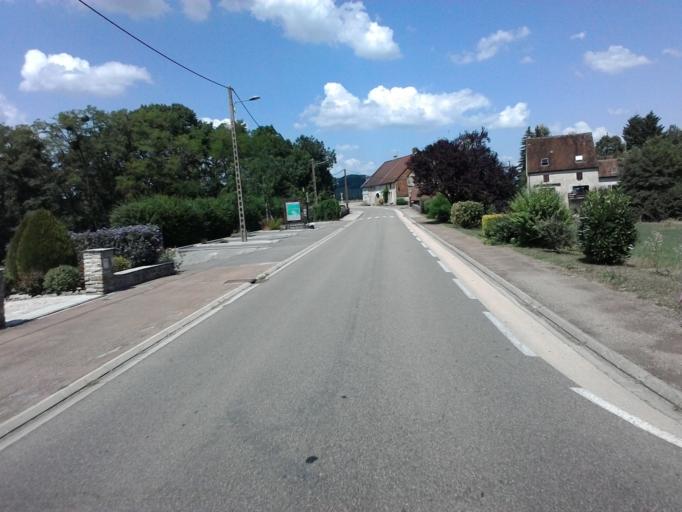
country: FR
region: Franche-Comte
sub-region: Departement du Jura
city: Montmorot
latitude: 46.7609
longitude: 5.5603
